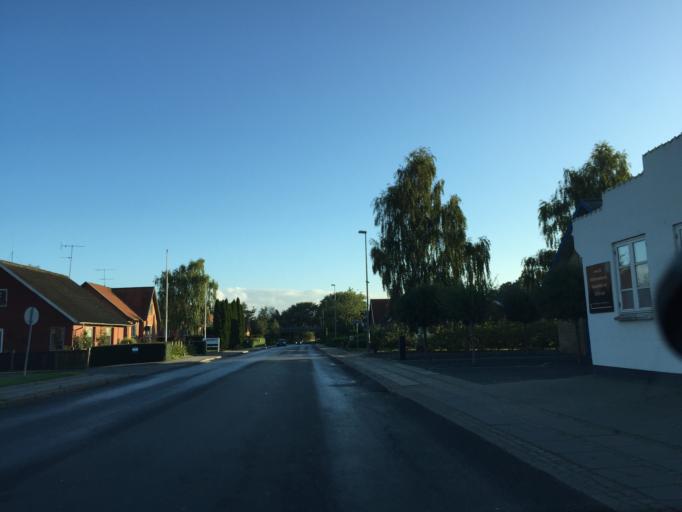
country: DK
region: Central Jutland
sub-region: Viborg Kommune
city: Bjerringbro
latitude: 56.3086
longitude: 9.5924
